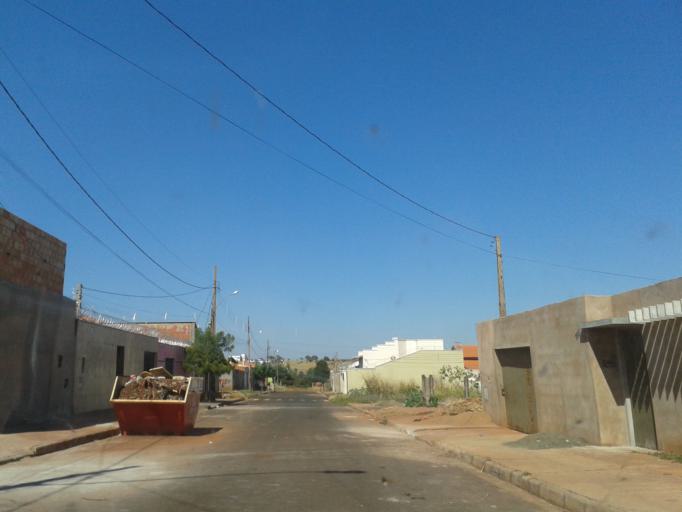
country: BR
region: Minas Gerais
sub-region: Ituiutaba
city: Ituiutaba
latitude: -18.9953
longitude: -49.4602
